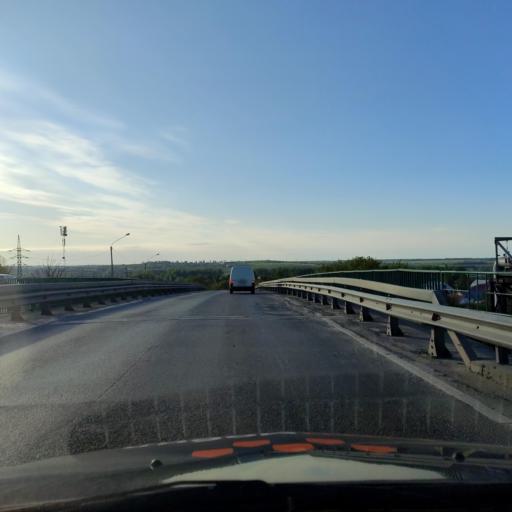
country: RU
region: Lipetsk
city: Yelets
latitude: 52.5917
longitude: 38.4923
